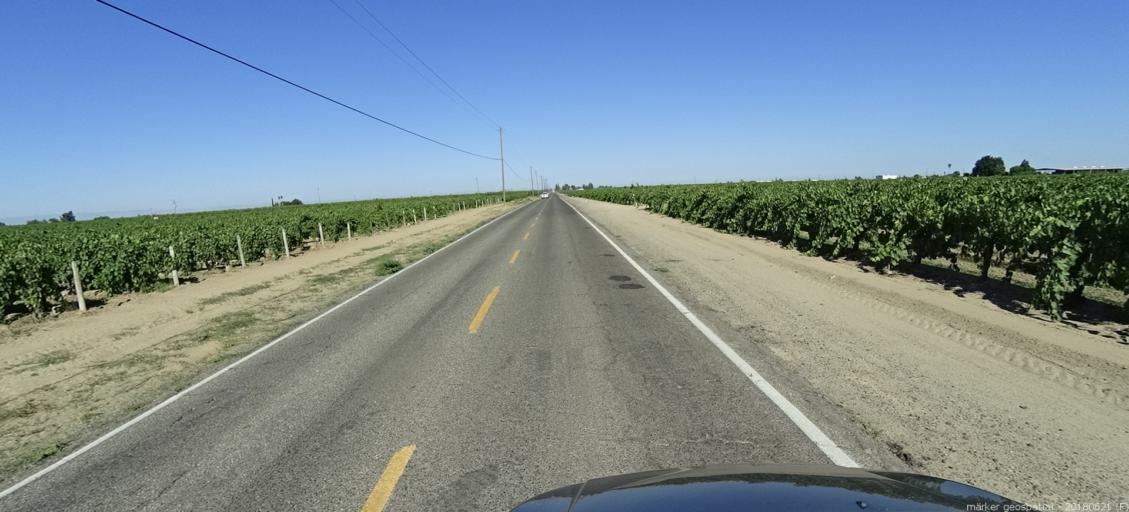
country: US
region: California
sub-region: Fresno County
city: Biola
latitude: 36.8514
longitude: -120.0116
